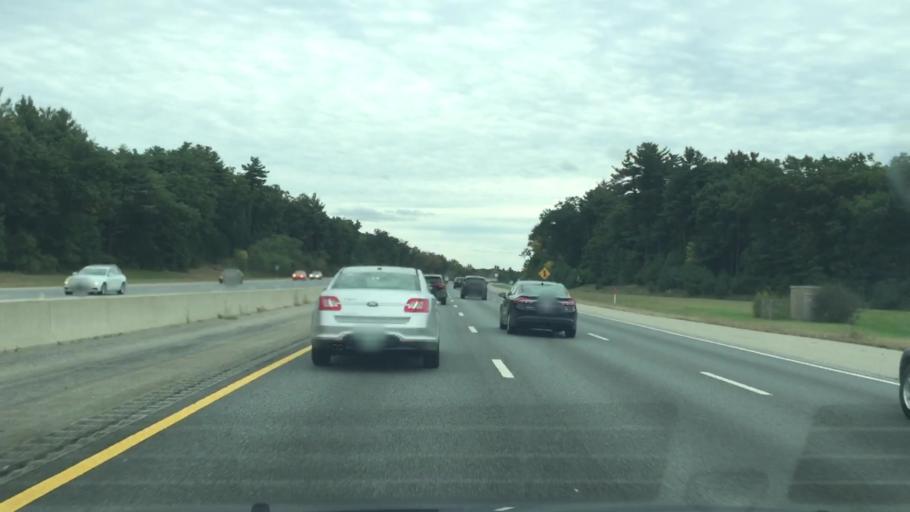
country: US
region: Massachusetts
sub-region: Middlesex County
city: Lowell
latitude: 42.5881
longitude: -71.3124
